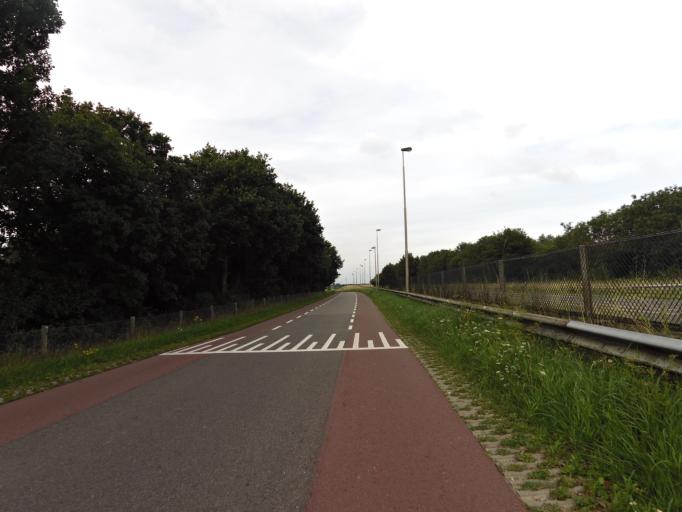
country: NL
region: Gelderland
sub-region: Gemeente Doesburg
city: Doesburg
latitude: 52.0030
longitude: 6.1504
